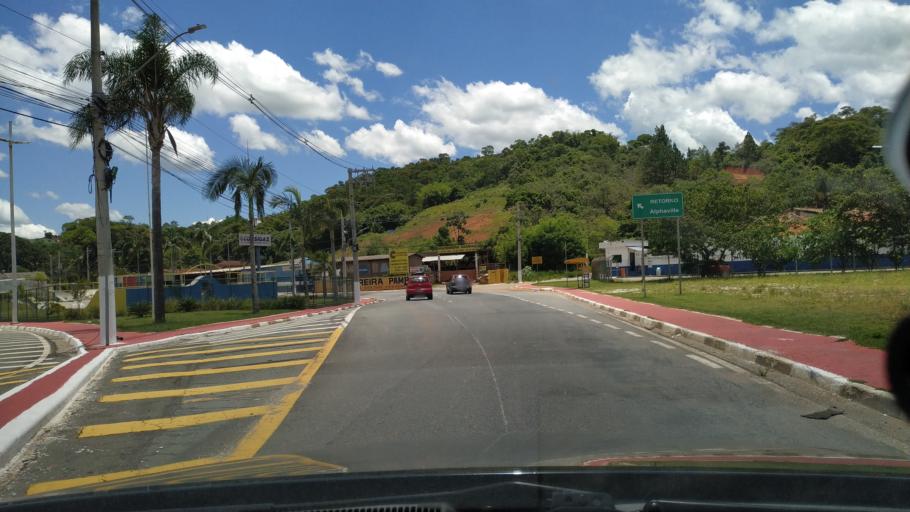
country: BR
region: Sao Paulo
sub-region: Santana De Parnaiba
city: Santana de Parnaiba
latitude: -23.4396
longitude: -46.9100
